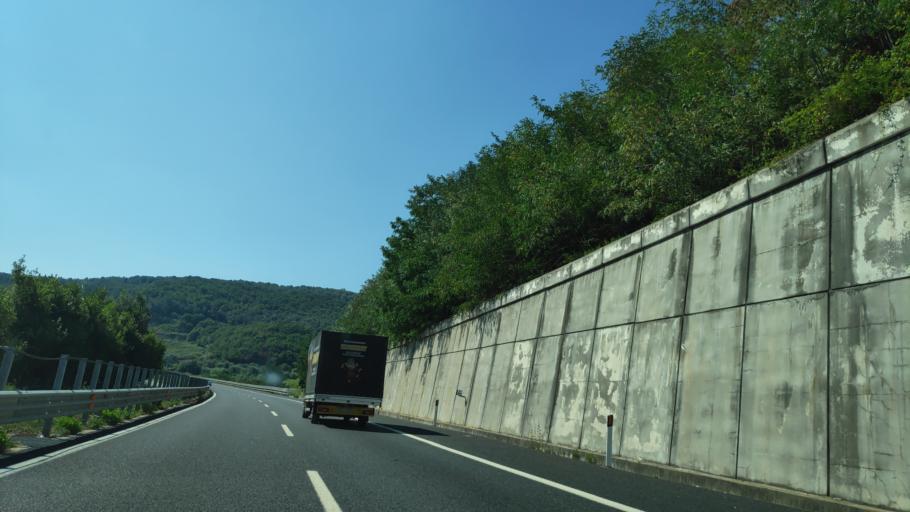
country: IT
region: Calabria
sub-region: Provincia di Reggio Calabria
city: Seminara
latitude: 38.3585
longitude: 15.8652
